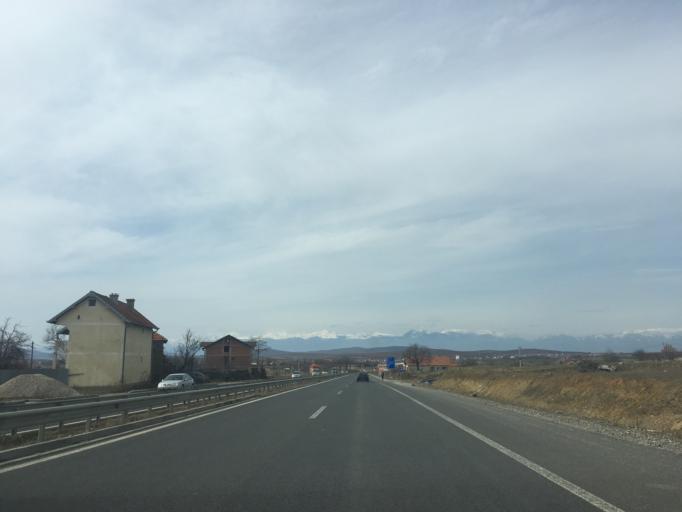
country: XK
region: Prizren
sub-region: Komuna e Malisheves
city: Llazice
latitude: 42.5666
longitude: 20.7575
